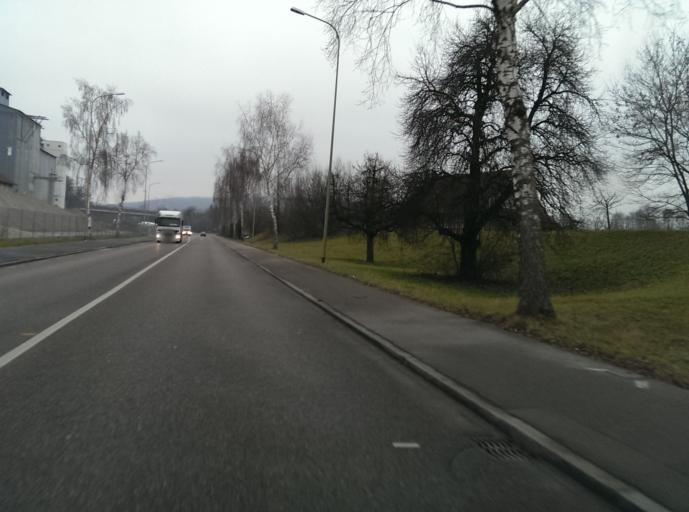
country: CH
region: Zurich
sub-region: Bezirk Dietikon
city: Dietikon / Hofacker
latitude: 47.4049
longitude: 8.4145
